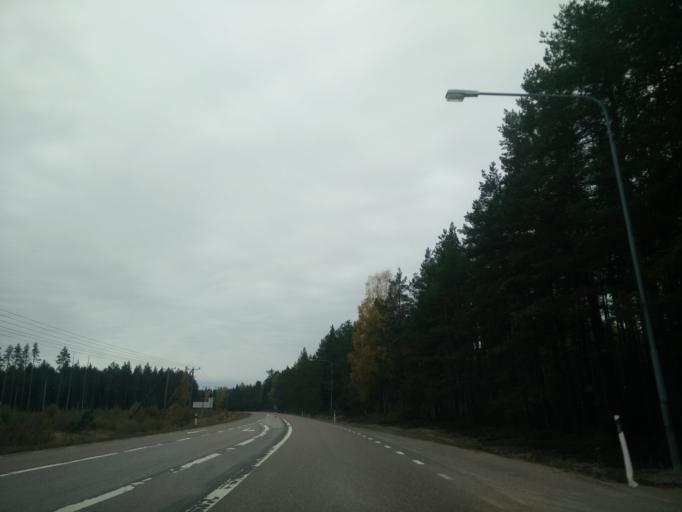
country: SE
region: Gaevleborg
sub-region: Gavle Kommun
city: Gavle
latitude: 60.7892
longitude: 17.2029
